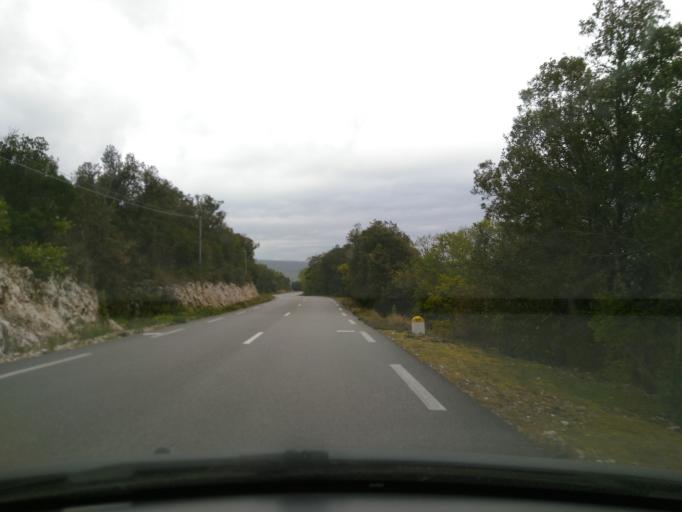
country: FR
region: Languedoc-Roussillon
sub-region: Departement du Gard
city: Barjac
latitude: 44.3383
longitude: 4.4161
